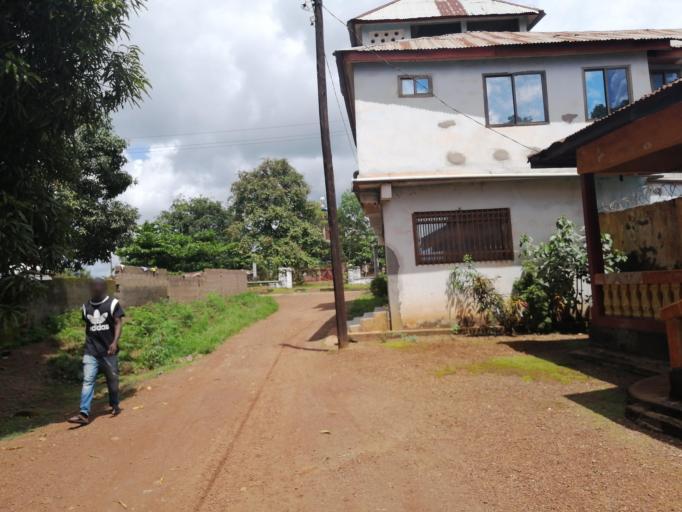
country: SL
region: Northern Province
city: Port Loko
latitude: 8.7684
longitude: -12.7823
